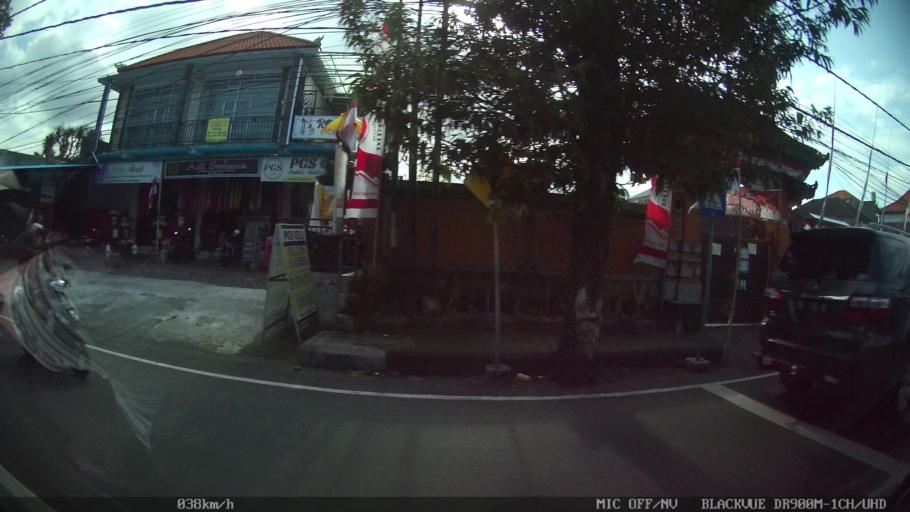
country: ID
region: Bali
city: Tabanan
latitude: -8.5491
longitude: 115.1238
